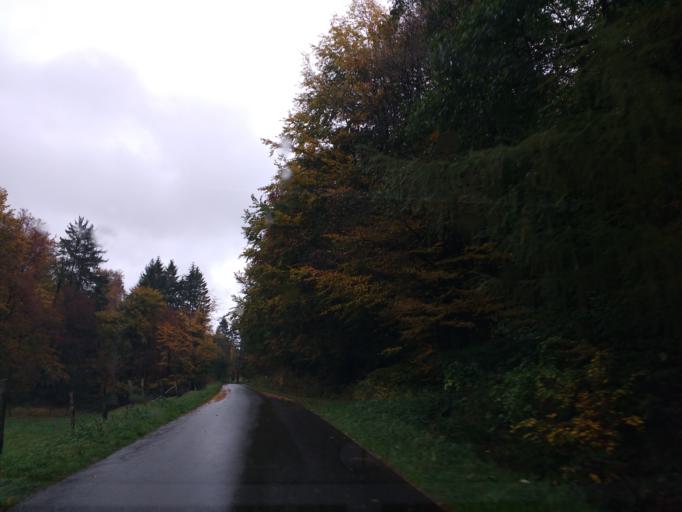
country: DE
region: Lower Saxony
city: Herzberg am Harz
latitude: 51.6356
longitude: 10.3902
